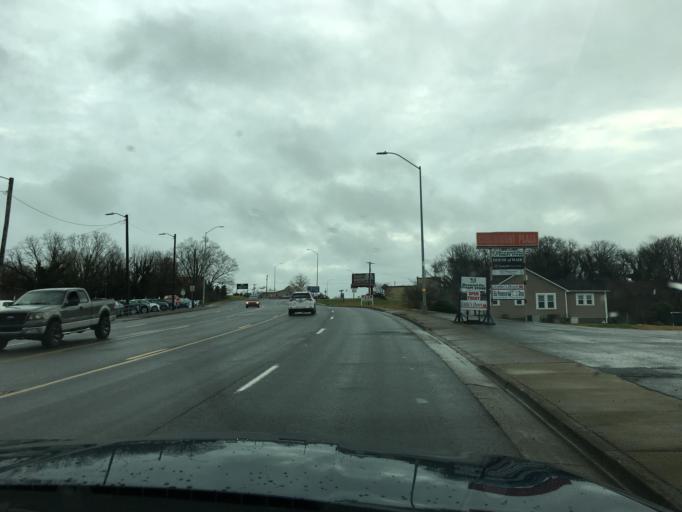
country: US
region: Tennessee
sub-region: McMinn County
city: Athens
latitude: 35.4483
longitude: -84.6026
